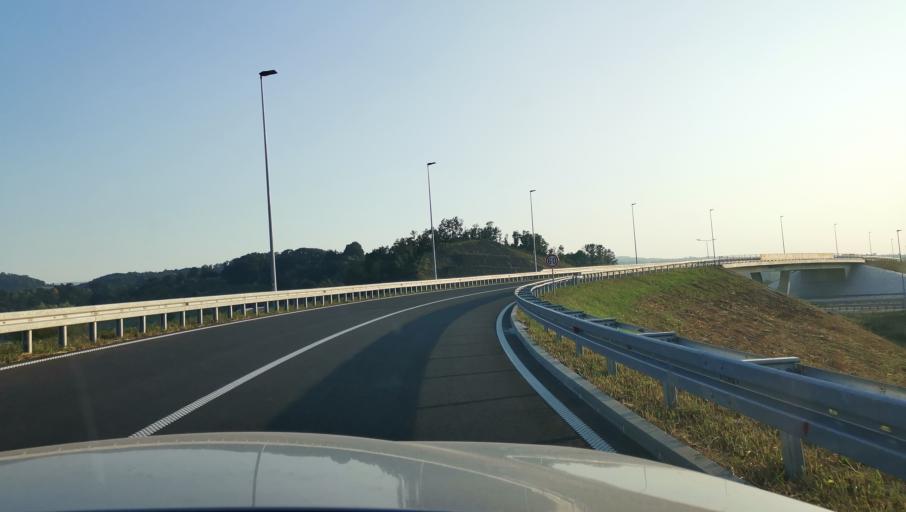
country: RS
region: Central Serbia
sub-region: Kolubarski Okrug
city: Ljig
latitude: 44.2334
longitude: 20.2558
